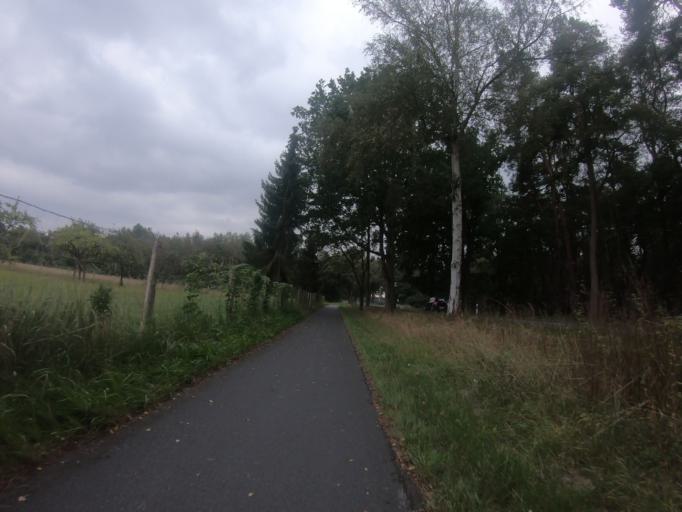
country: DE
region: Lower Saxony
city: Ribbesbuttel
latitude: 52.4458
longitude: 10.5015
